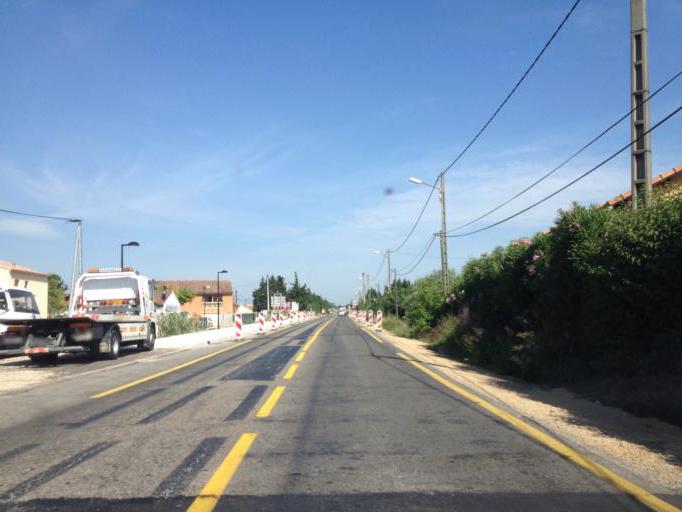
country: FR
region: Provence-Alpes-Cote d'Azur
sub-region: Departement du Vaucluse
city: Piolenc
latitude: 44.1807
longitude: 4.7580
